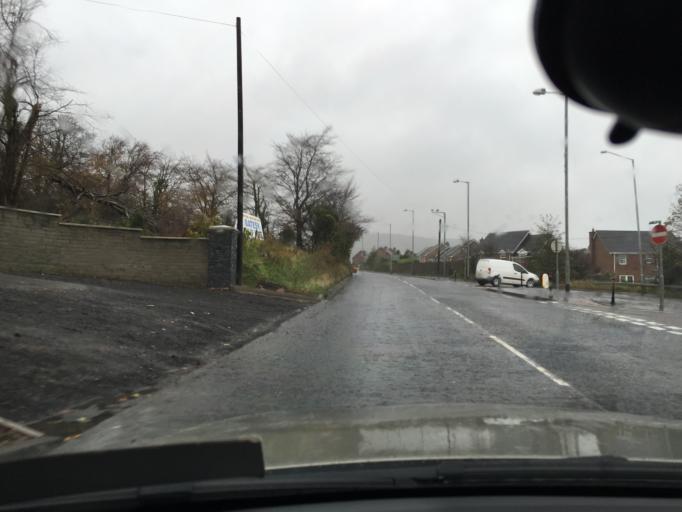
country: GB
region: Northern Ireland
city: Carnmoney
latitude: 54.6325
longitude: -5.9712
